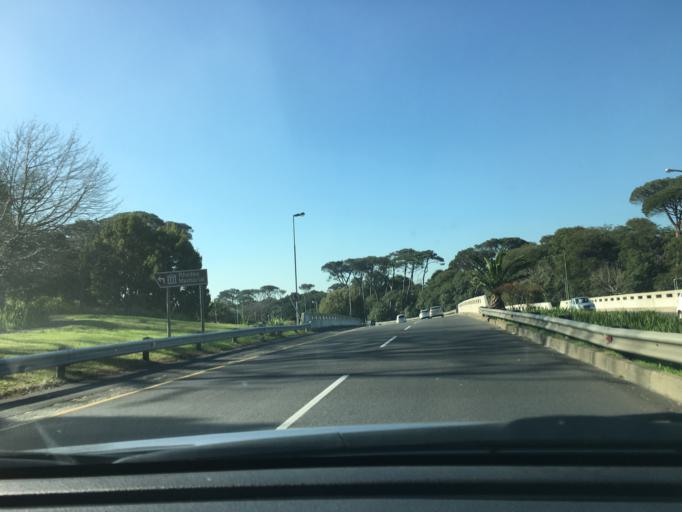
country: ZA
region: Western Cape
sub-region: City of Cape Town
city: Newlands
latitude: -33.9658
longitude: 18.4577
